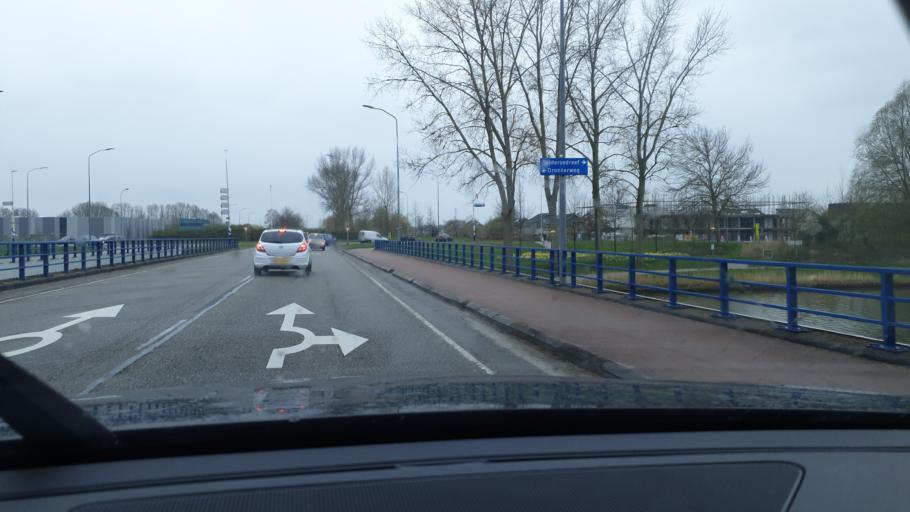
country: NL
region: Flevoland
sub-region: Gemeente Lelystad
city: Lelystad
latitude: 52.5006
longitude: 5.5105
